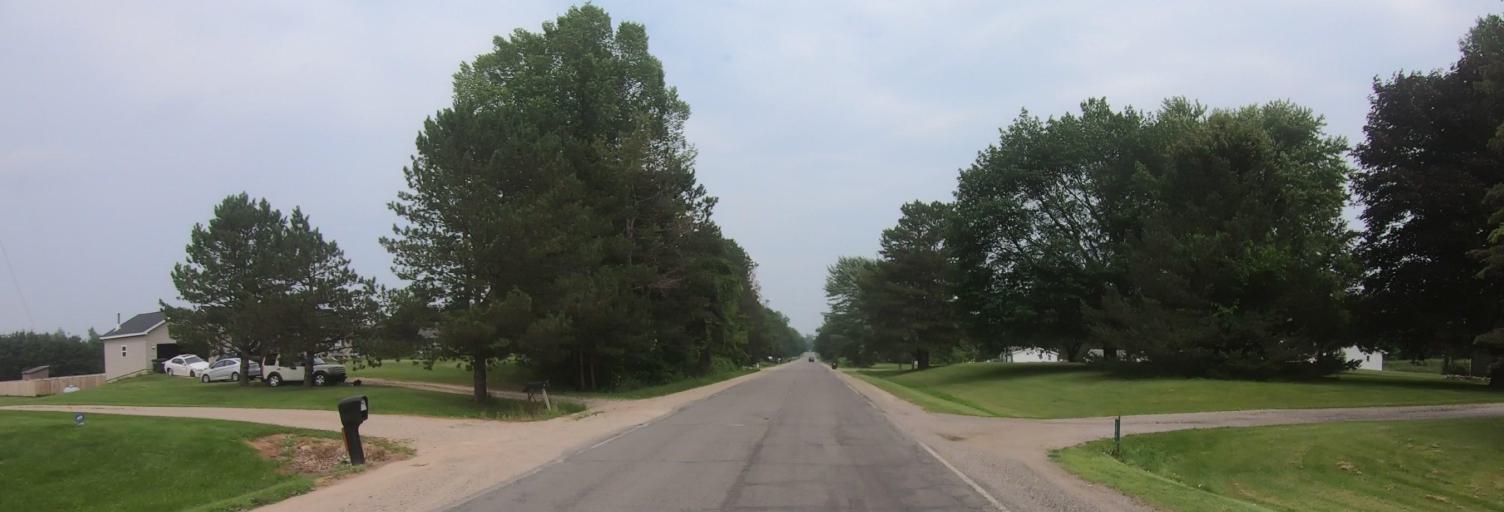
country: US
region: Michigan
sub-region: Shiawassee County
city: Perry
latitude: 42.8607
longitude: -84.1317
